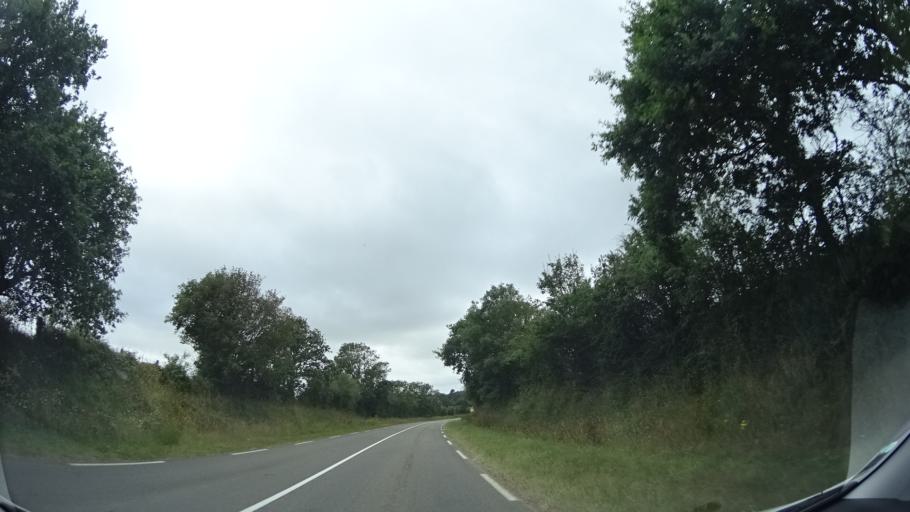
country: FR
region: Lower Normandy
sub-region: Departement de la Manche
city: Portbail
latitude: 49.3198
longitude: -1.6289
